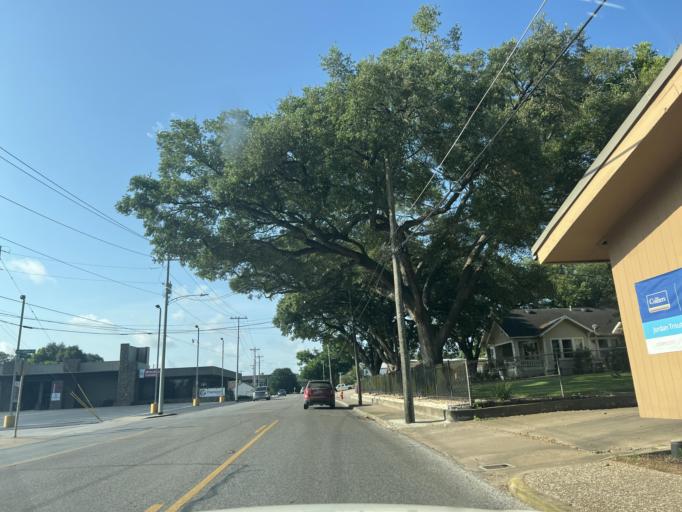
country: US
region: Texas
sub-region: Washington County
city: Brenham
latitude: 30.1542
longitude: -96.3926
